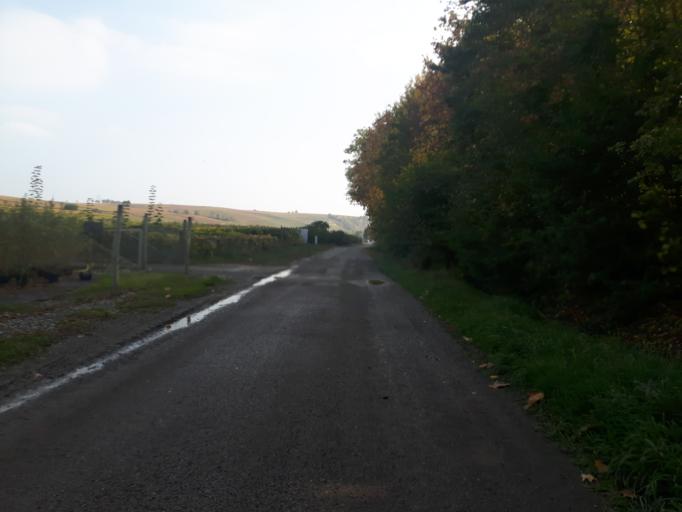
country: DE
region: Baden-Wuerttemberg
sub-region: Regierungsbezirk Stuttgart
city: Lauffen am Neckar
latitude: 49.0716
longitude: 9.1646
